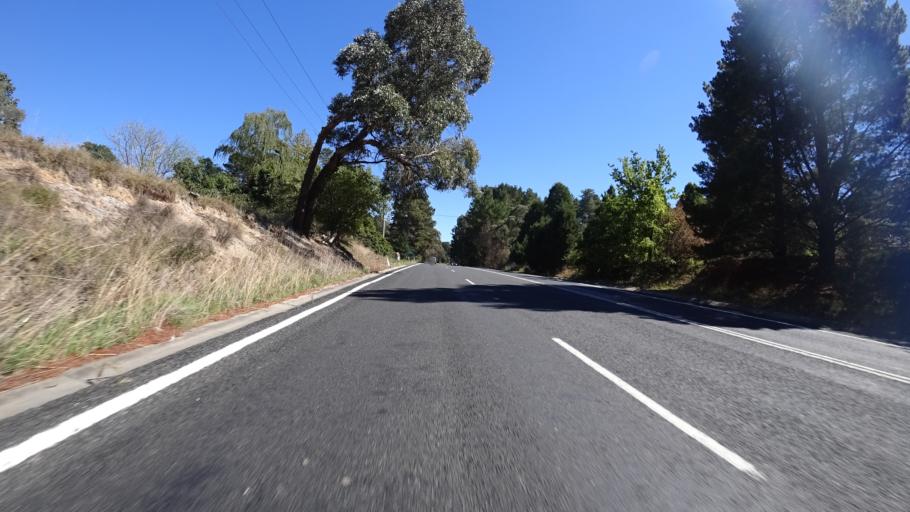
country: AU
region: New South Wales
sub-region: Lithgow
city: Portland
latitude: -33.3770
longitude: 150.0745
